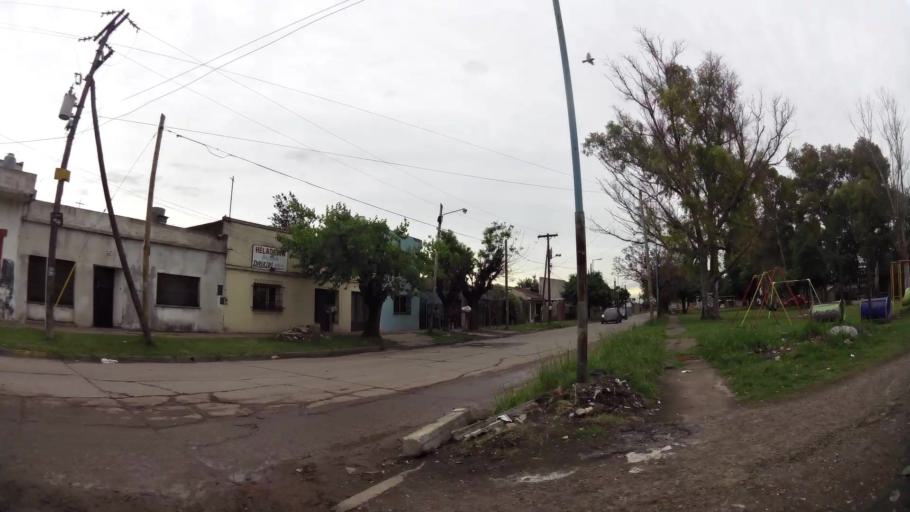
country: AR
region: Buenos Aires
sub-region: Partido de Lanus
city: Lanus
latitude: -34.7234
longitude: -58.3535
